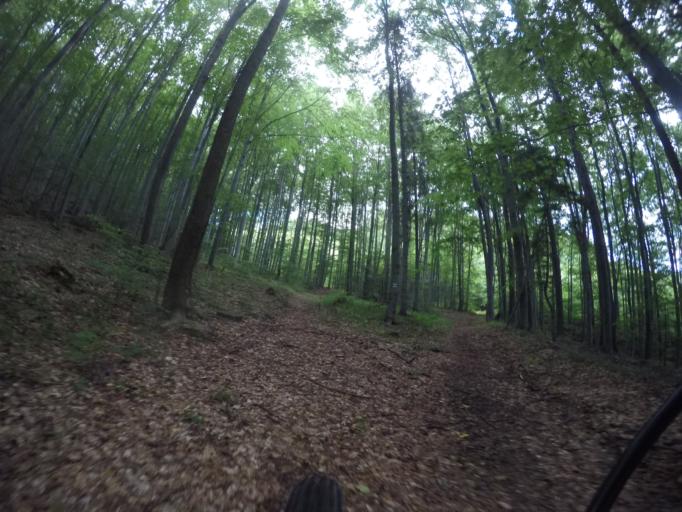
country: SK
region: Kosicky
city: Gelnica
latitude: 48.9253
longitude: 21.0244
